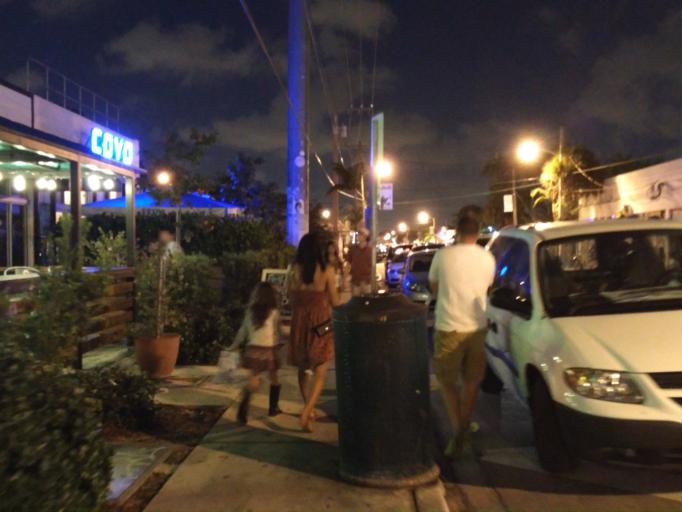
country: US
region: Florida
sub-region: Miami-Dade County
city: Miami
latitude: 25.7996
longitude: -80.1991
